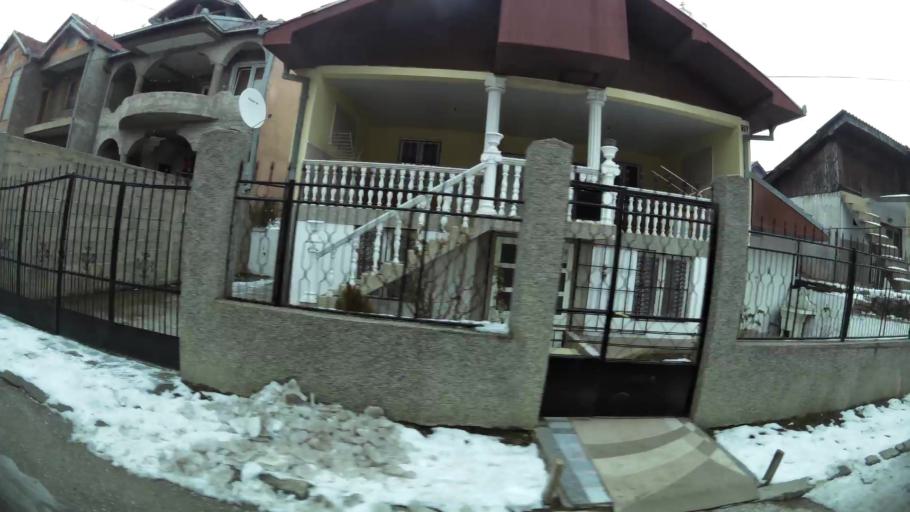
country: MK
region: Suto Orizari
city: Suto Orizare
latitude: 42.0383
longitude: 21.4219
